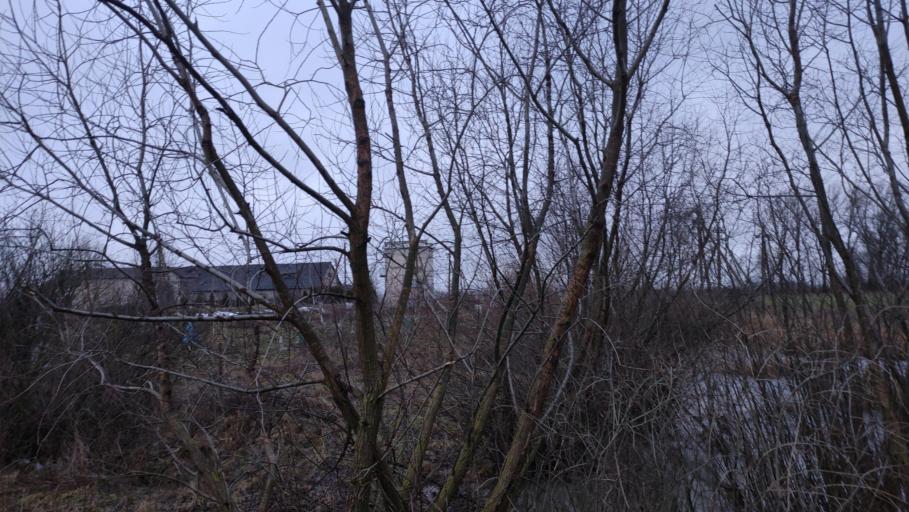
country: LT
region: Alytaus apskritis
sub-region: Alytus
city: Alytus
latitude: 54.4076
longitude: 23.9442
